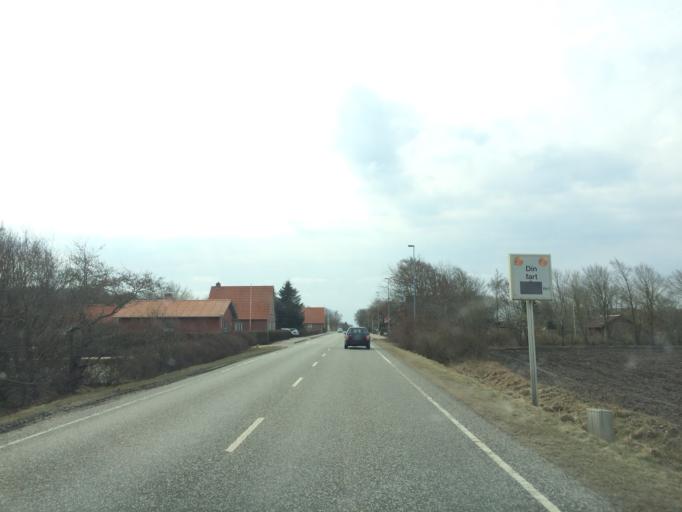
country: DK
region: Central Jutland
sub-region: Ringkobing-Skjern Kommune
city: Skjern
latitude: 56.0196
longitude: 8.5026
